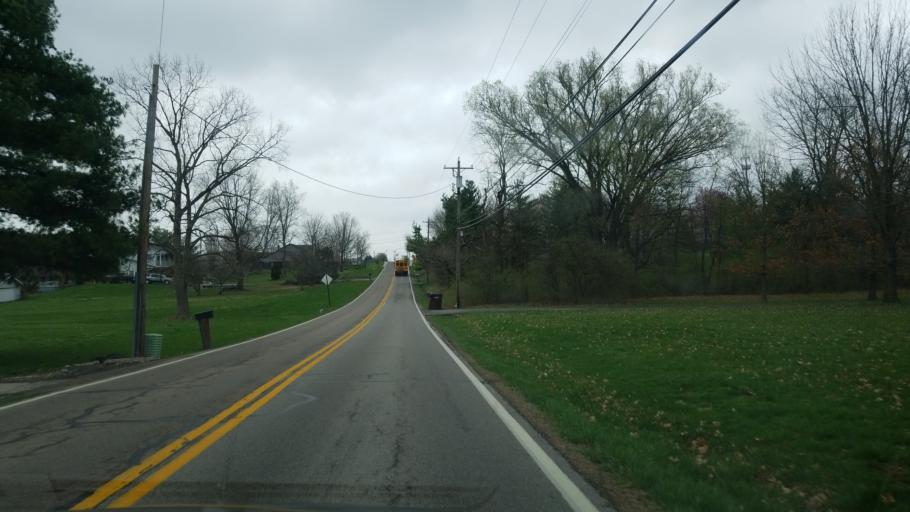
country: US
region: Ohio
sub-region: Butler County
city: Beckett Ridge
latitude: 39.3724
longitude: -84.4283
